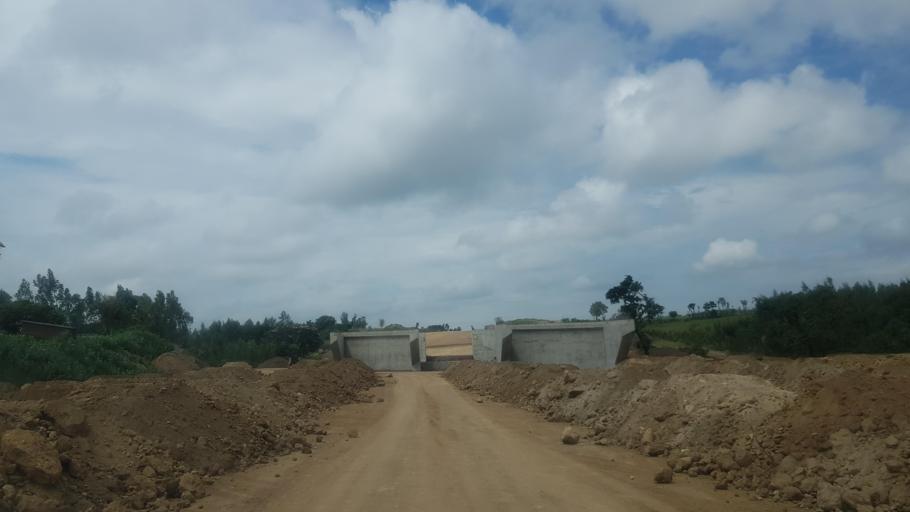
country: ET
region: Oromiya
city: Shashemene
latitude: 7.2501
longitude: 38.5904
